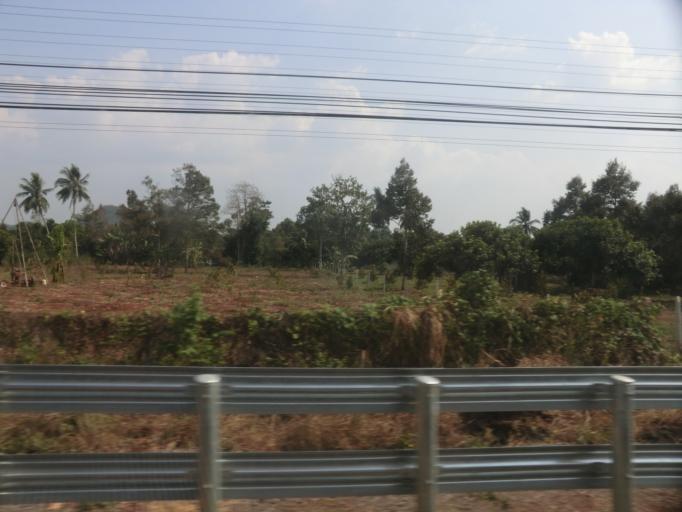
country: VN
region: Dong Nai
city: Long Khanh
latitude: 10.9298
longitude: 107.2050
